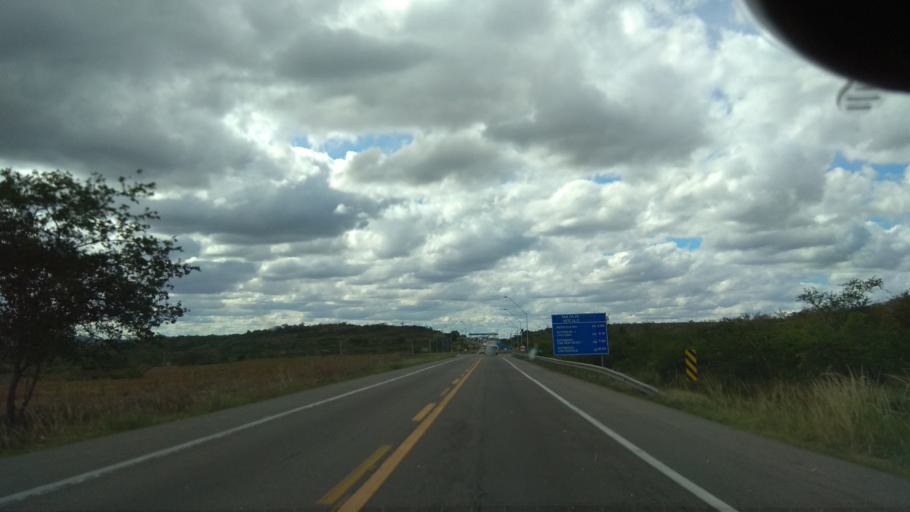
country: BR
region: Bahia
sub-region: Santa Ines
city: Santa Ines
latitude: -13.0170
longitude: -39.9591
